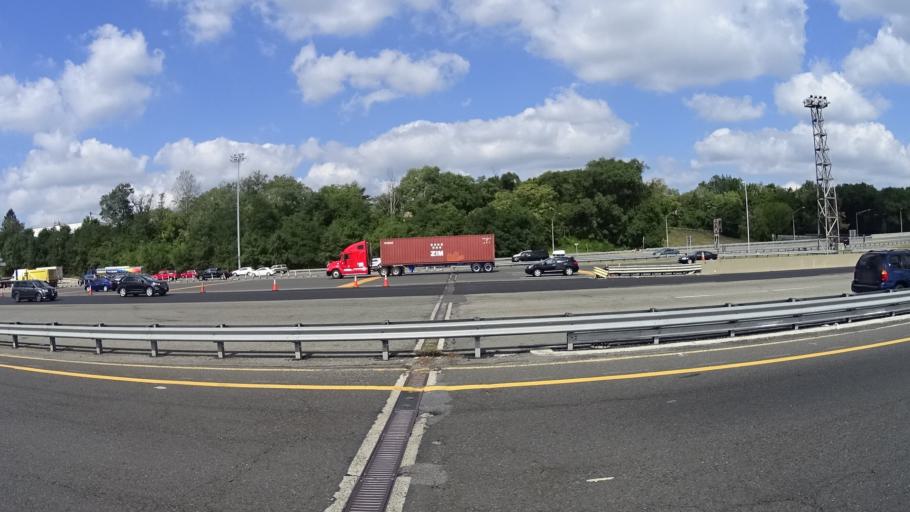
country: US
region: New Jersey
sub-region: Hudson County
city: Secaucus
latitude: 40.7784
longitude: -74.0571
